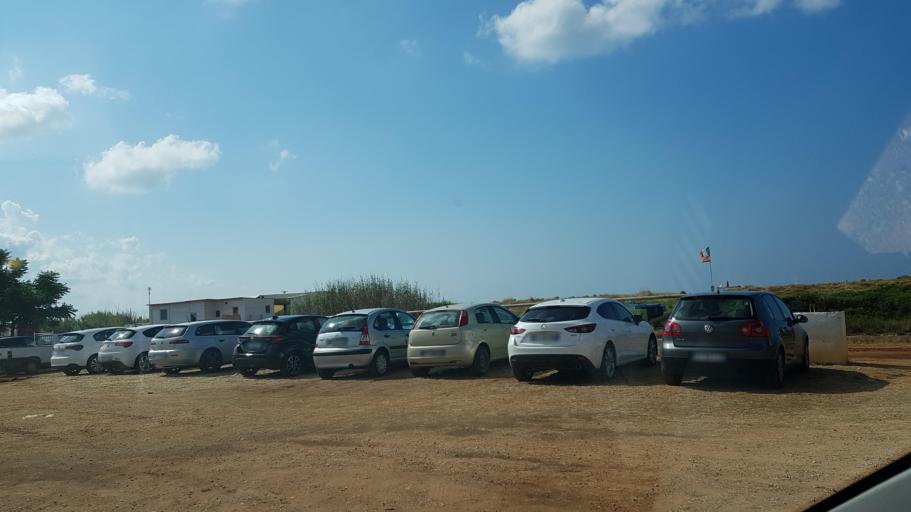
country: IT
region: Apulia
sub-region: Provincia di Lecce
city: Salve
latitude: 39.8369
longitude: 18.2296
